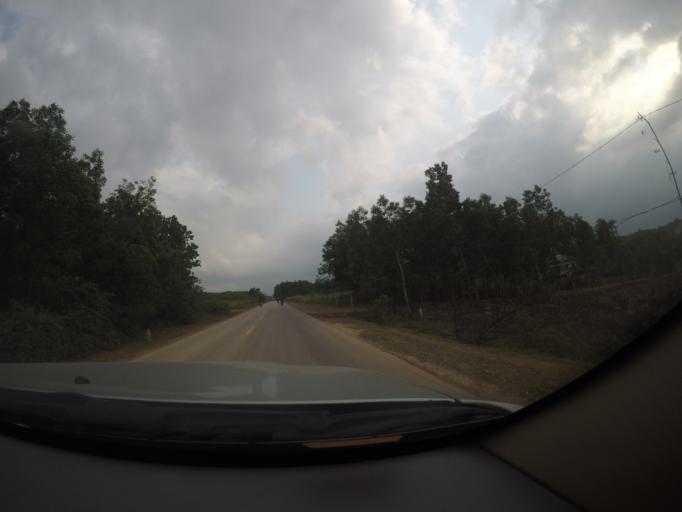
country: VN
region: Quang Tri
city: Ho Xa
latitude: 17.0639
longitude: 106.8611
